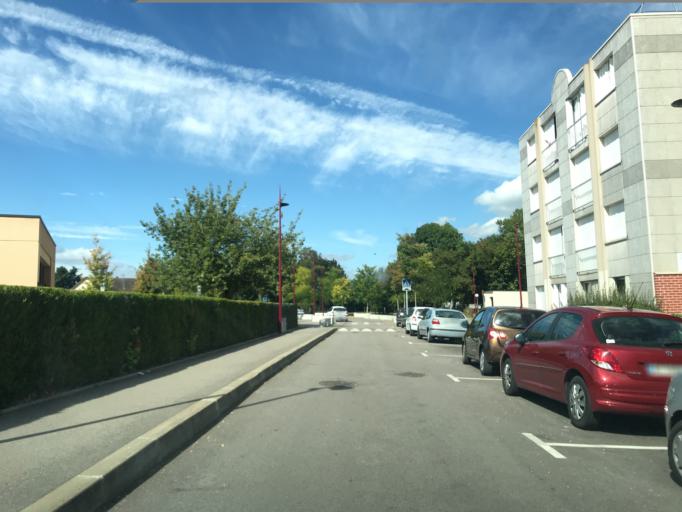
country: FR
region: Haute-Normandie
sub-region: Departement de l'Eure
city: Gaillon
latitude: 49.1591
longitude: 1.3449
